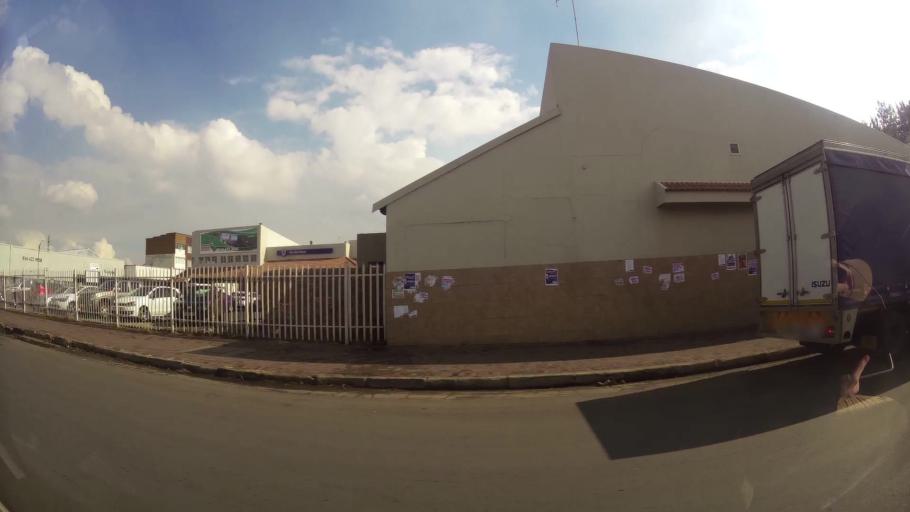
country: ZA
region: Gauteng
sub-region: Sedibeng District Municipality
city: Vereeniging
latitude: -26.6697
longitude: 27.9327
